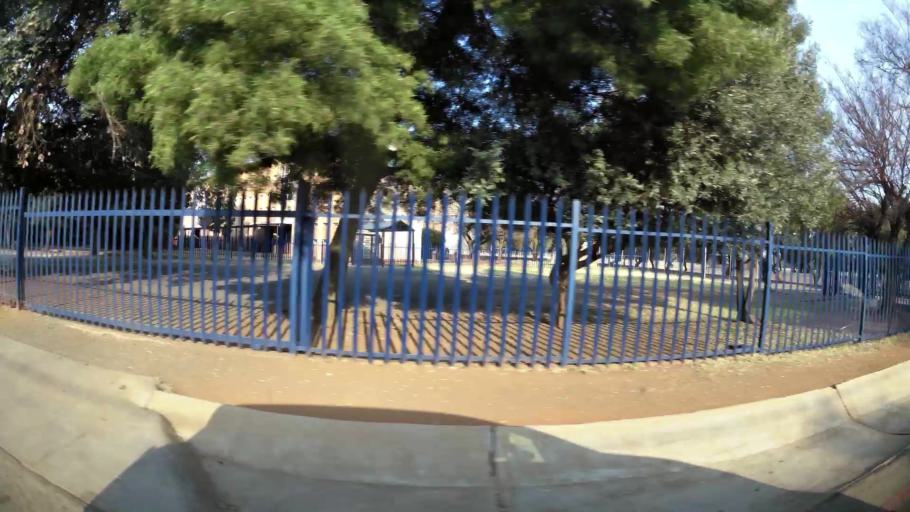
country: ZA
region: Gauteng
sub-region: Ekurhuleni Metropolitan Municipality
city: Benoni
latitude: -26.1086
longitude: 28.3720
